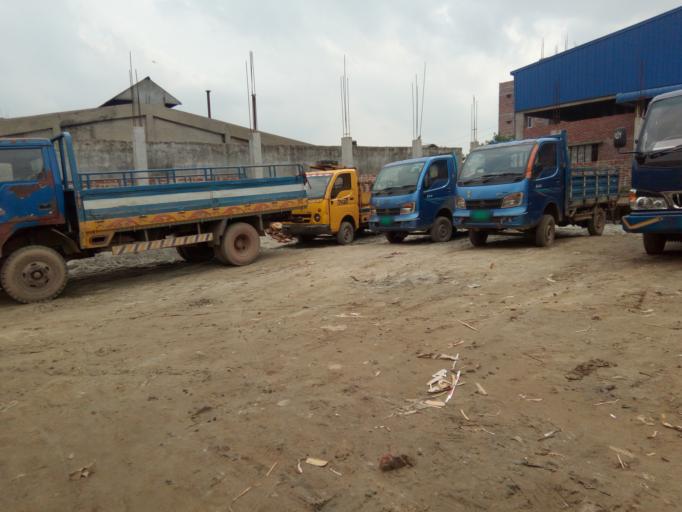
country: BD
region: Dhaka
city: Paltan
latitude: 23.7133
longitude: 90.4501
